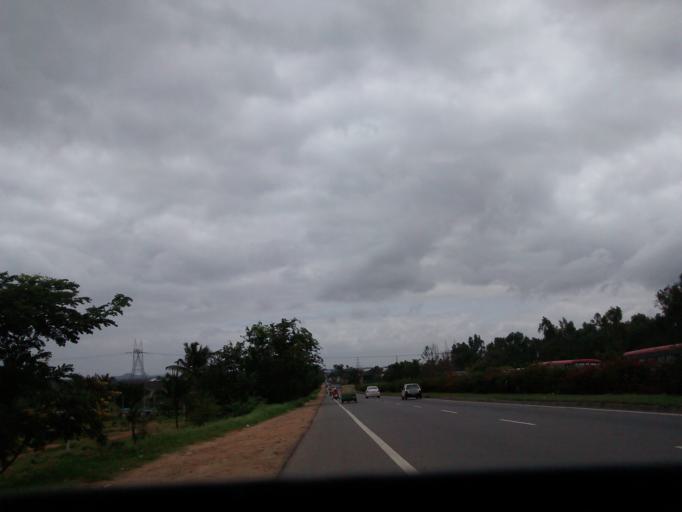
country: IN
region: Karnataka
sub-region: Bangalore Rural
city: Nelamangala
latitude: 13.1228
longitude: 77.3667
